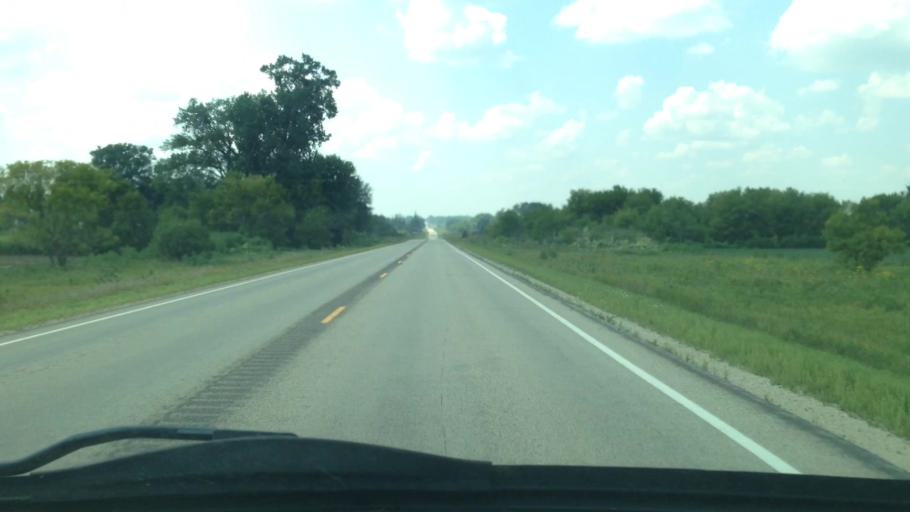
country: US
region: Minnesota
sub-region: Olmsted County
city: Stewartville
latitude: 43.8555
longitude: -92.4300
